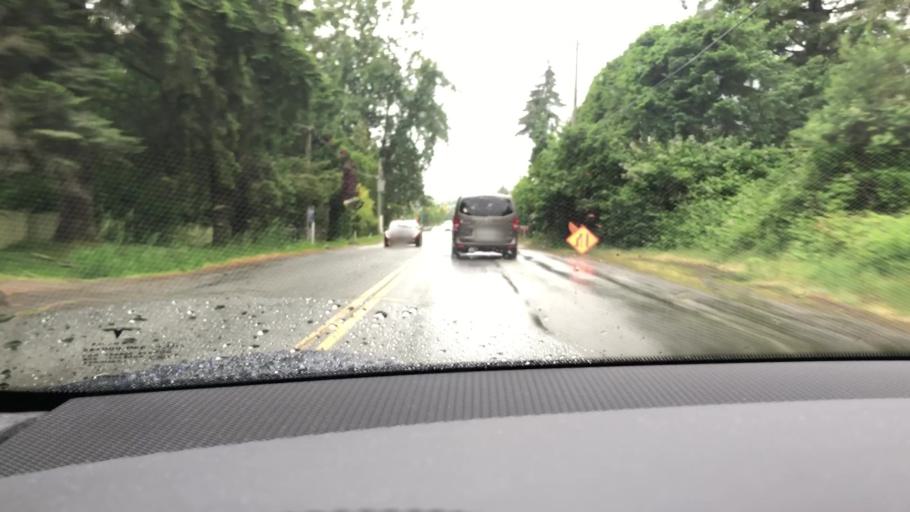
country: CA
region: British Columbia
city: Langley
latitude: 49.1335
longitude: -122.6583
